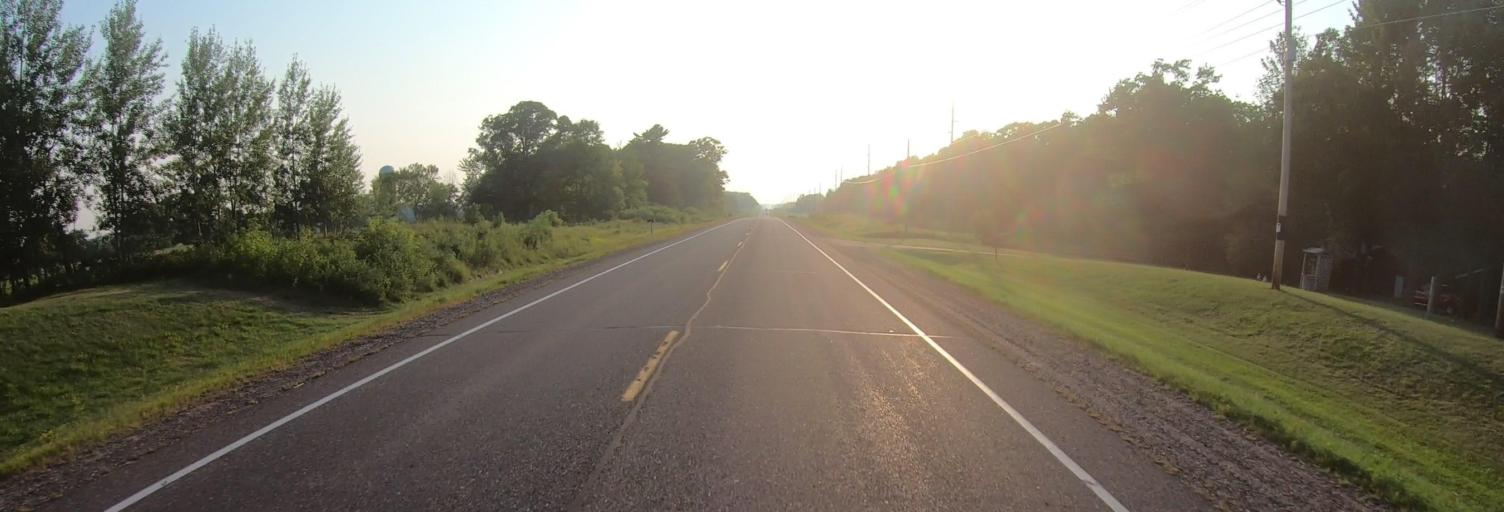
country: US
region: Wisconsin
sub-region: Washburn County
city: Shell Lake
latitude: 45.8155
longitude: -92.0369
